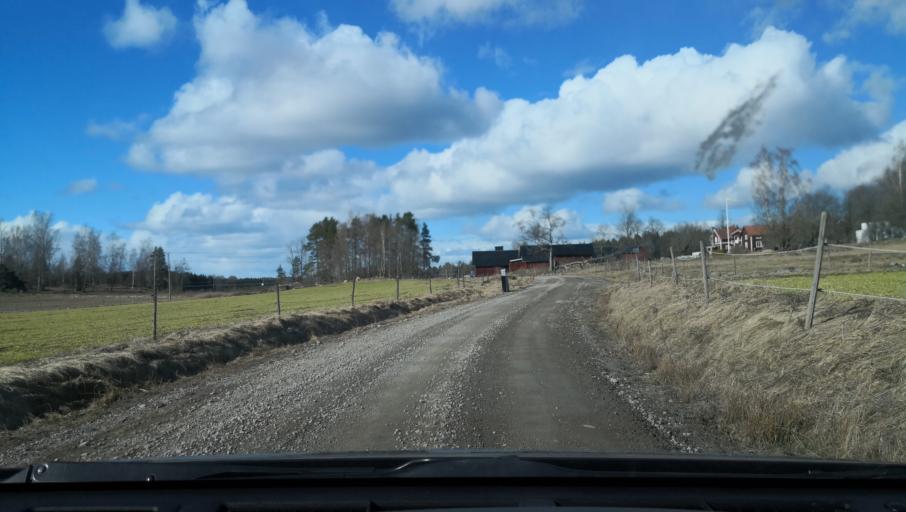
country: SE
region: OErebro
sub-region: Lindesbergs Kommun
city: Fellingsbro
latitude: 59.4233
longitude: 15.6274
